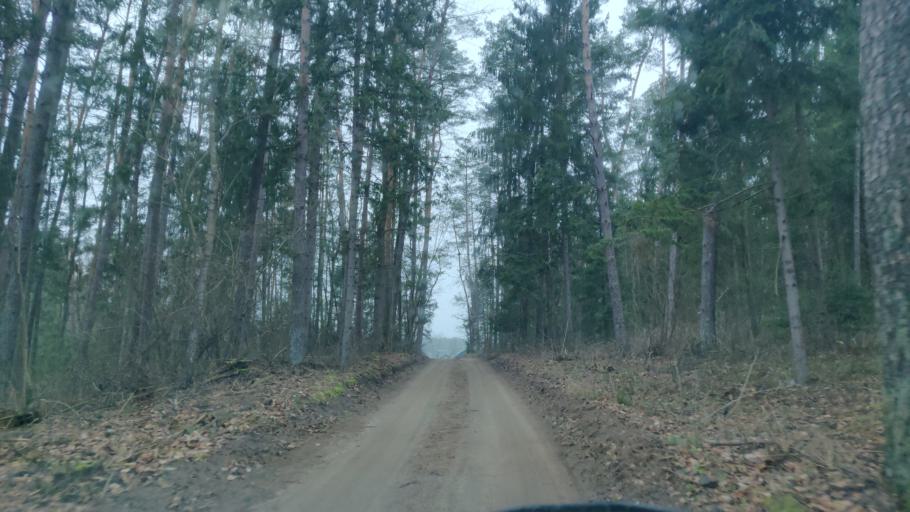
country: LT
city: Trakai
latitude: 54.5585
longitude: 24.9349
